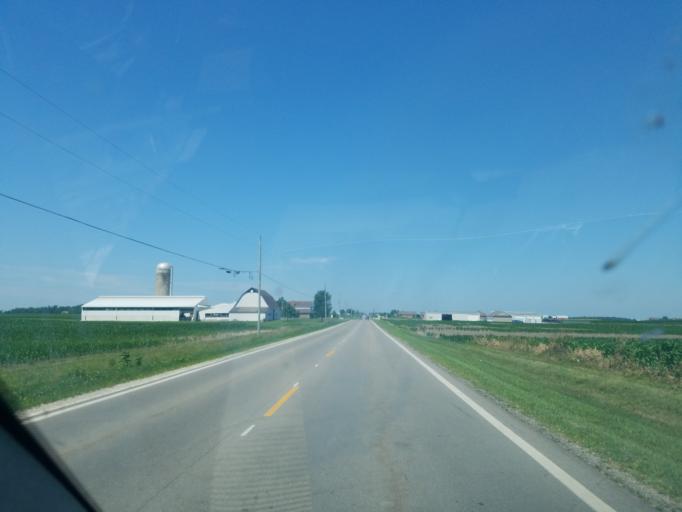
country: US
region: Ohio
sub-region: Auglaize County
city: Minster
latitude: 40.4076
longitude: -84.4390
